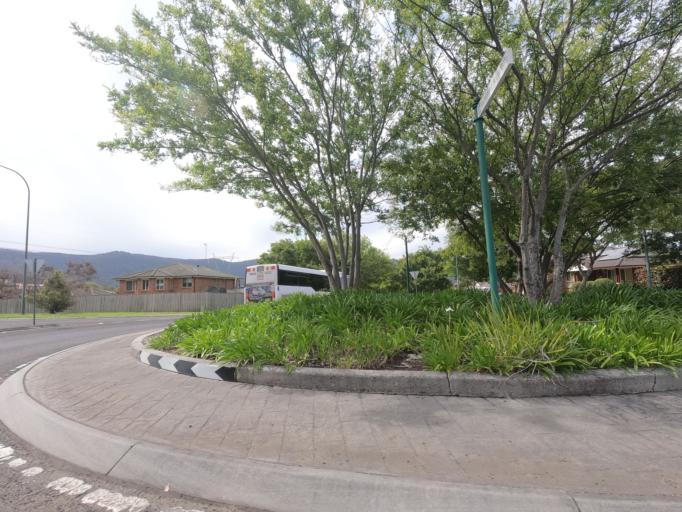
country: AU
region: New South Wales
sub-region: Wollongong
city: Dapto
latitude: -34.4917
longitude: 150.7688
